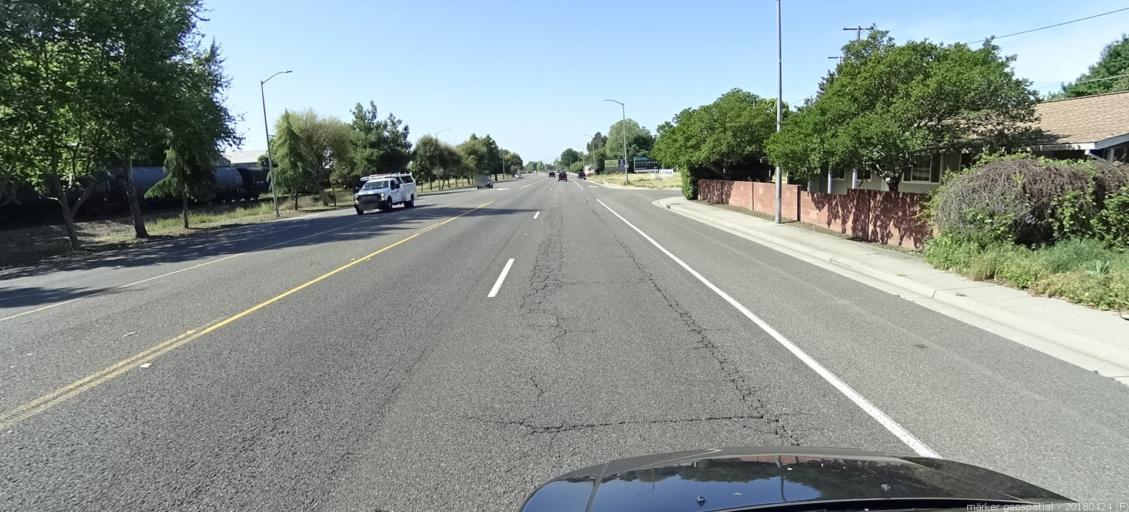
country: US
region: California
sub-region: Yolo County
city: West Sacramento
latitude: 38.5663
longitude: -121.5262
